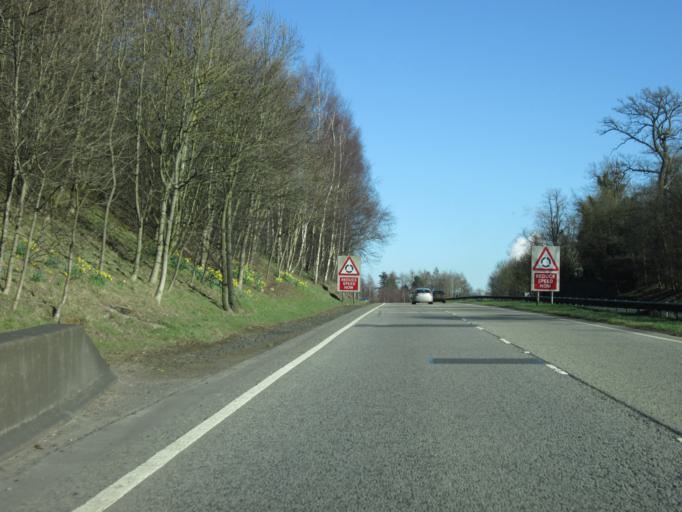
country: GB
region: England
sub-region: Northumberland
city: Hexham
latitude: 54.9825
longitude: -2.1009
